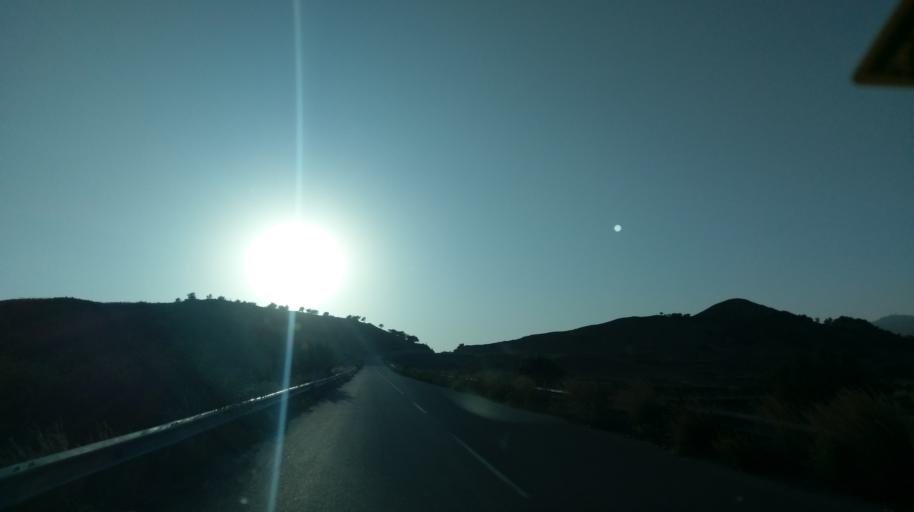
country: CY
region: Ammochostos
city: Trikomo
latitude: 35.3685
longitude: 33.9476
